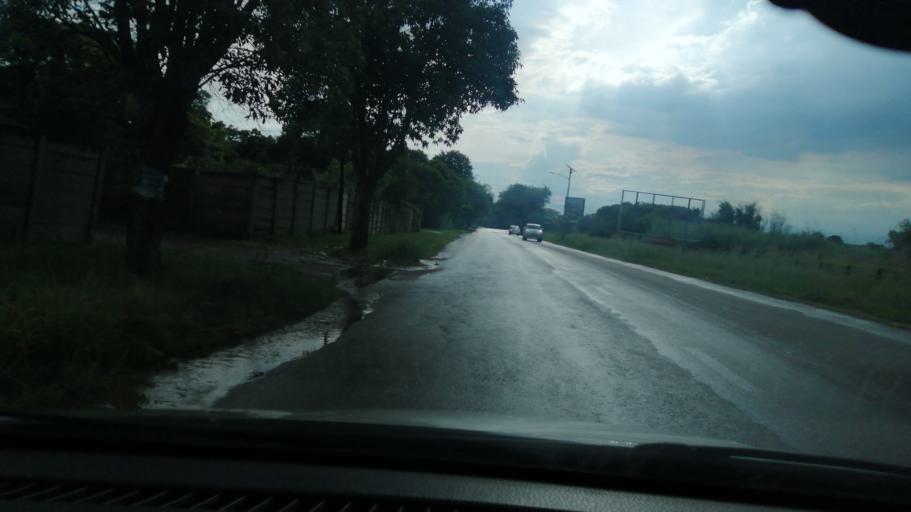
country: ZW
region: Harare
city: Harare
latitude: -17.7894
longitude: 31.0520
